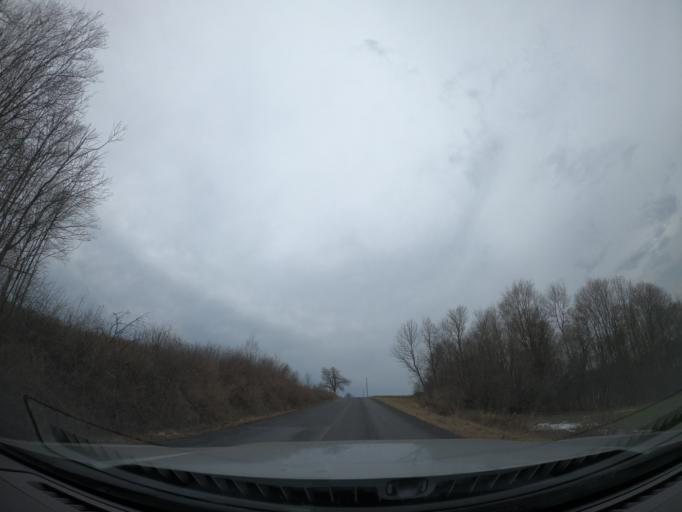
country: US
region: New York
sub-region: Cayuga County
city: Melrose Park
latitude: 42.8402
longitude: -76.5314
